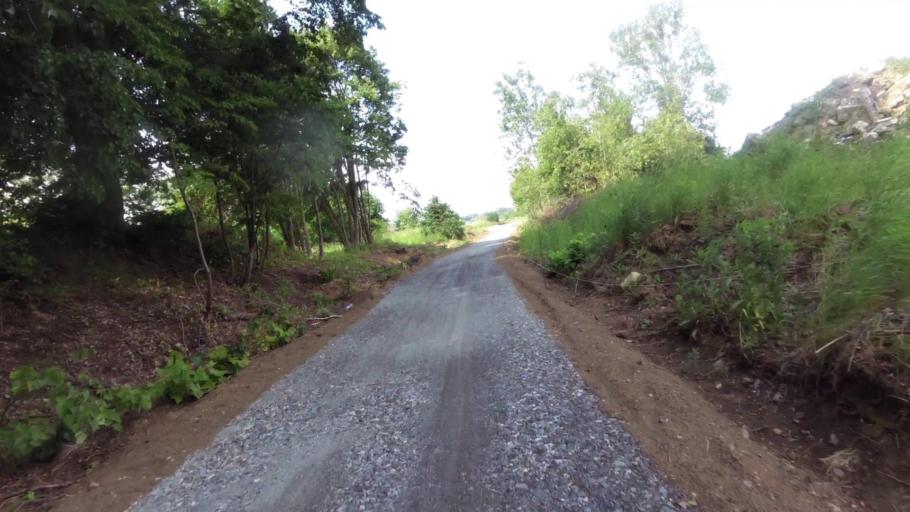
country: PL
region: West Pomeranian Voivodeship
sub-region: Powiat pyrzycki
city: Bielice
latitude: 53.2098
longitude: 14.6124
